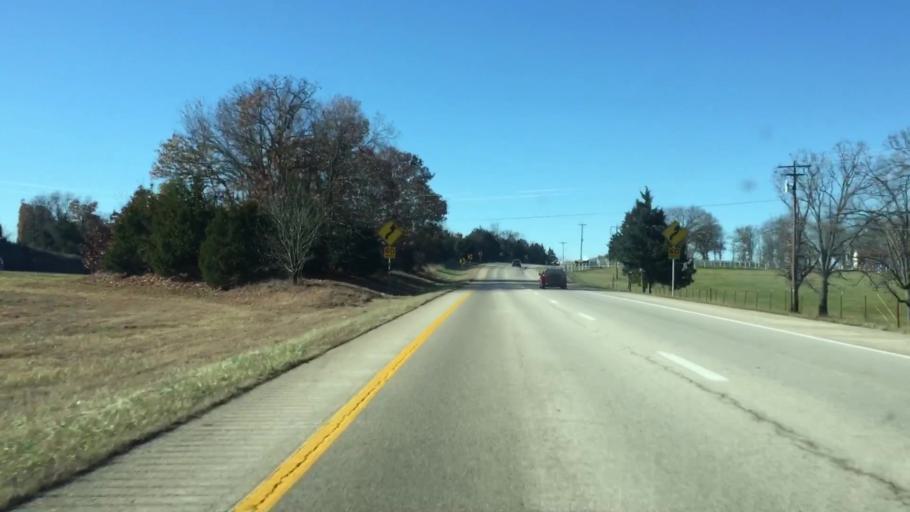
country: US
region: Missouri
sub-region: Cole County
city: Wardsville
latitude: 38.4336
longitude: -92.3137
